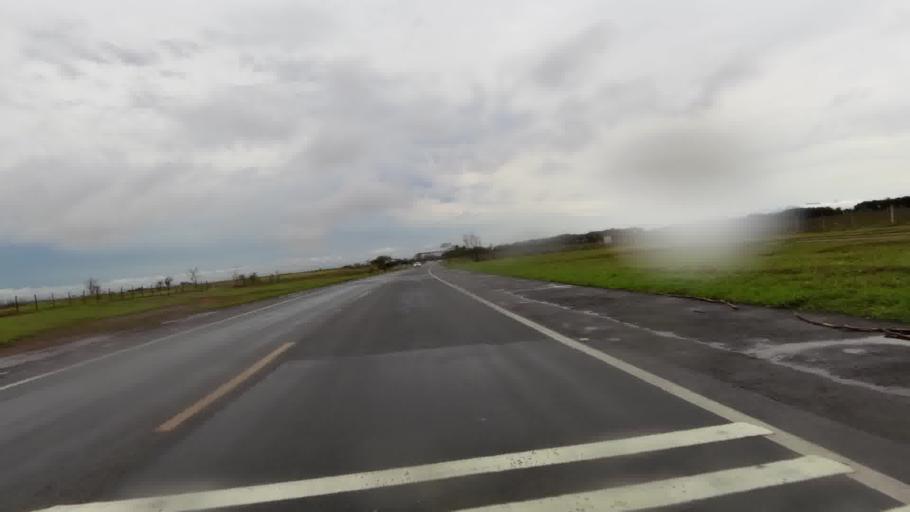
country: BR
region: Rio de Janeiro
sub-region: Campos Dos Goytacazes
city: Campos
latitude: -21.5315
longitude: -41.3395
